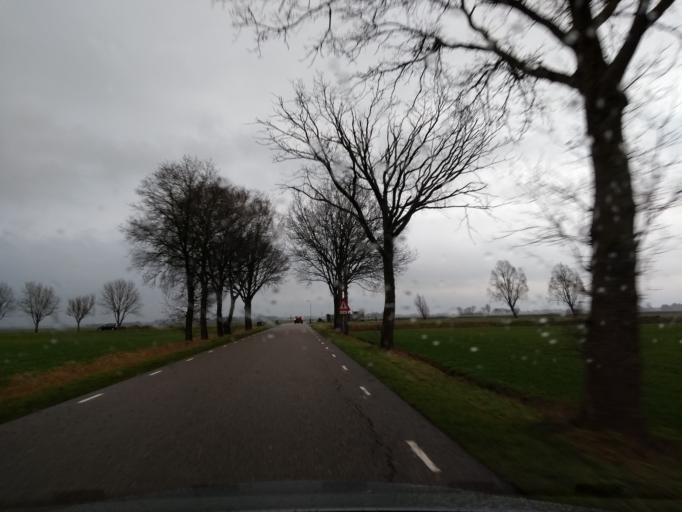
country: NL
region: Drenthe
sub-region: Gemeente Westerveld
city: Havelte
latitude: 52.7639
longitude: 6.2553
